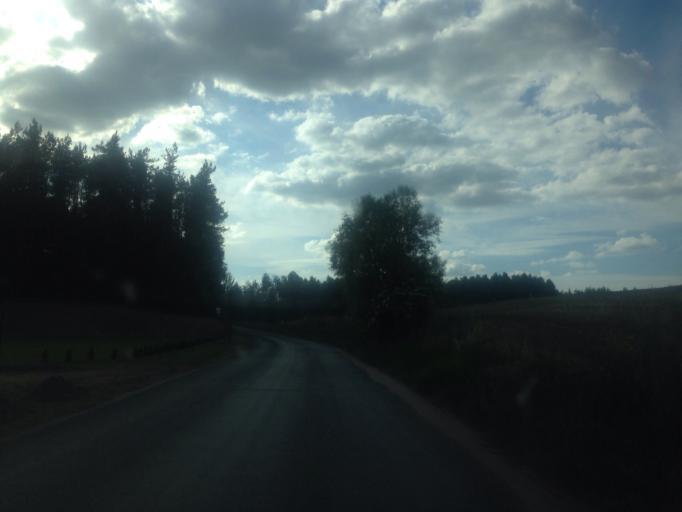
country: PL
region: Kujawsko-Pomorskie
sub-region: Powiat brodnicki
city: Brzozie
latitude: 53.3107
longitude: 19.5601
